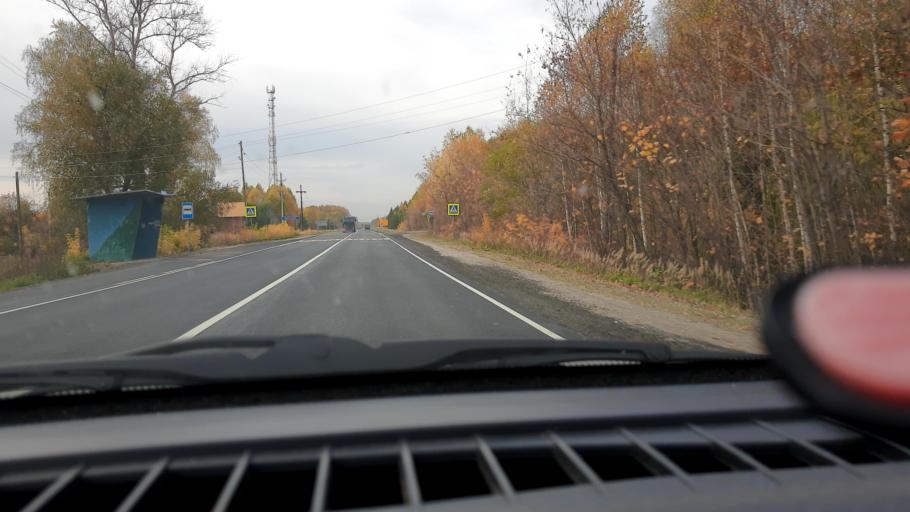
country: RU
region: Nizjnij Novgorod
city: Novaya Balakhna
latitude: 56.5980
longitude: 43.6406
